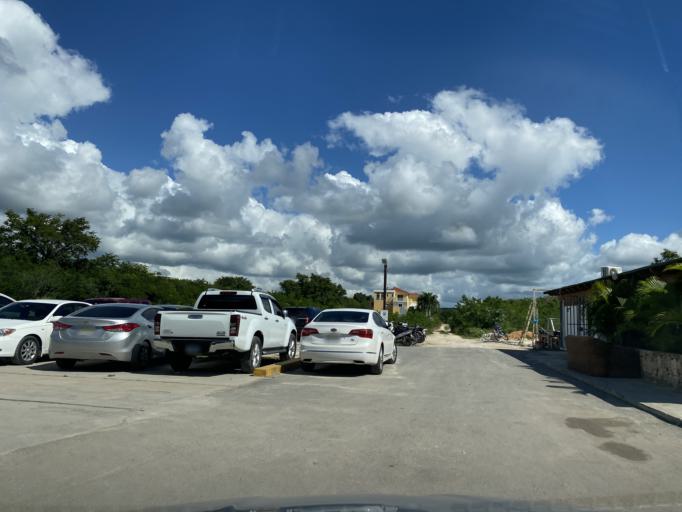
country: DO
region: La Romana
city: La Romana
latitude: 18.3527
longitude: -68.8341
